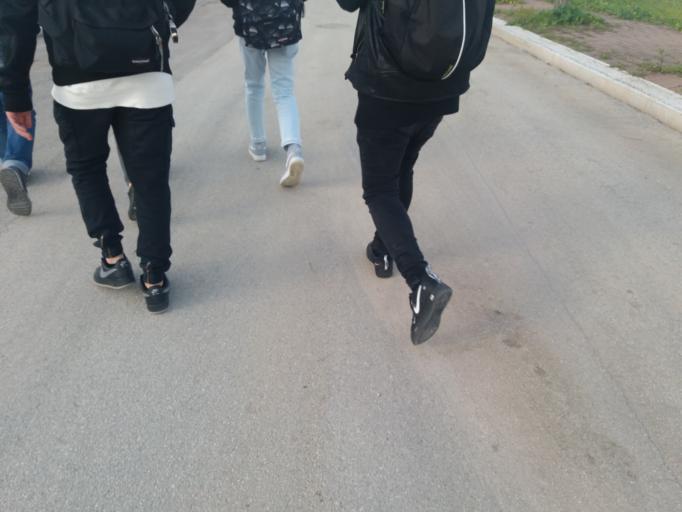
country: IT
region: Apulia
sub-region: Provincia di Barletta - Andria - Trani
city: Andria
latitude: 41.2386
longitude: 16.2910
